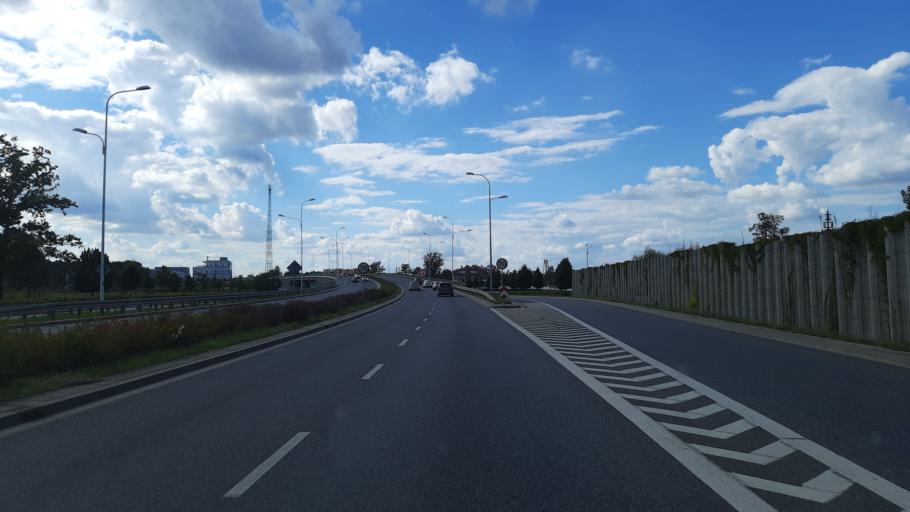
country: PL
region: Lower Silesian Voivodeship
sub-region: Powiat trzebnicki
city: Psary
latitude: 51.1579
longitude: 17.0160
